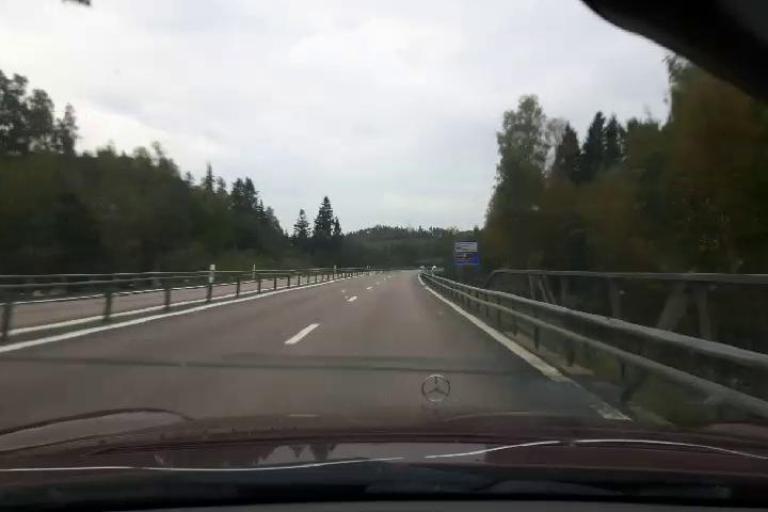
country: SE
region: Vaesternorrland
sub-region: Haernoesands Kommun
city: Haernoesand
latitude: 62.8170
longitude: 17.9684
